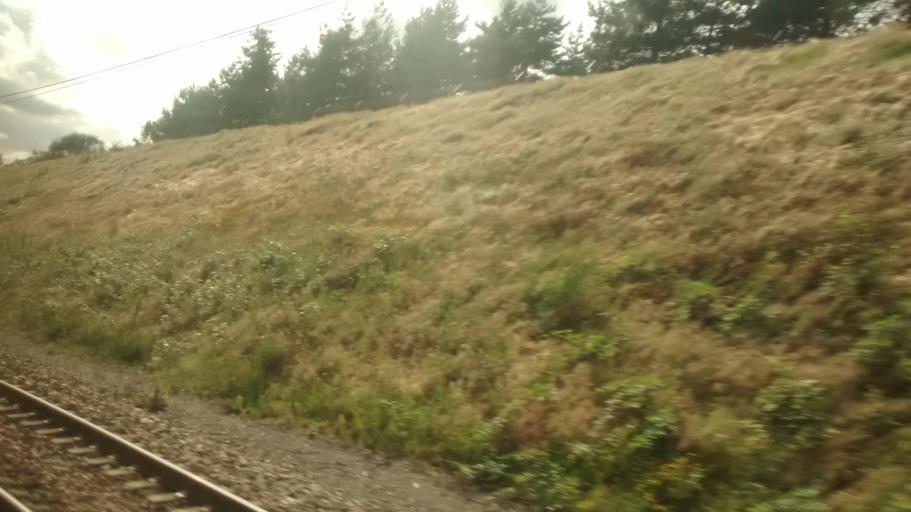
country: FR
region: Ile-de-France
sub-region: Departement de l'Essonne
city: Angervilliers
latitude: 48.5920
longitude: 2.0439
